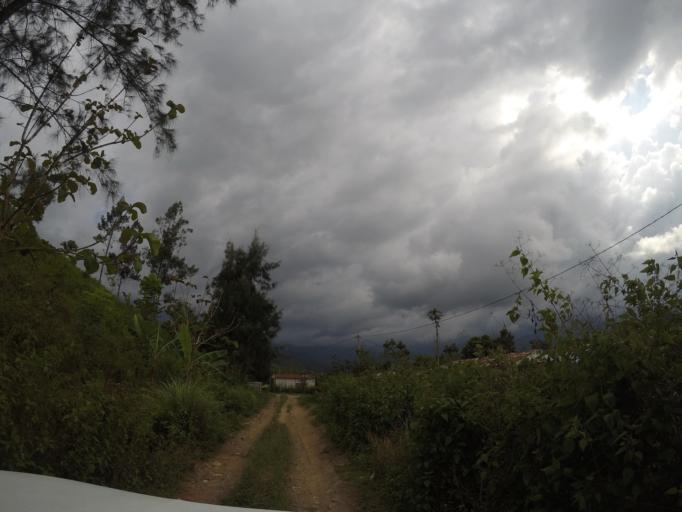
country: TL
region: Ermera
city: Gleno
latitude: -8.7084
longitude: 125.4518
